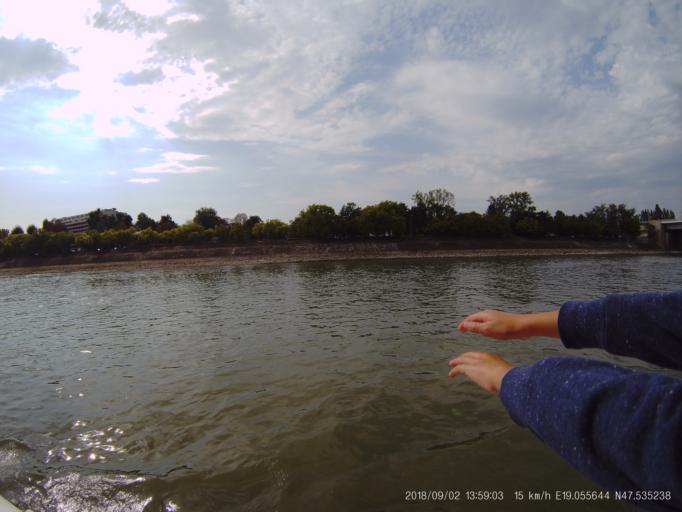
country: HU
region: Budapest
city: Budapest III. keruelet
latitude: 47.5353
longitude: 19.0557
